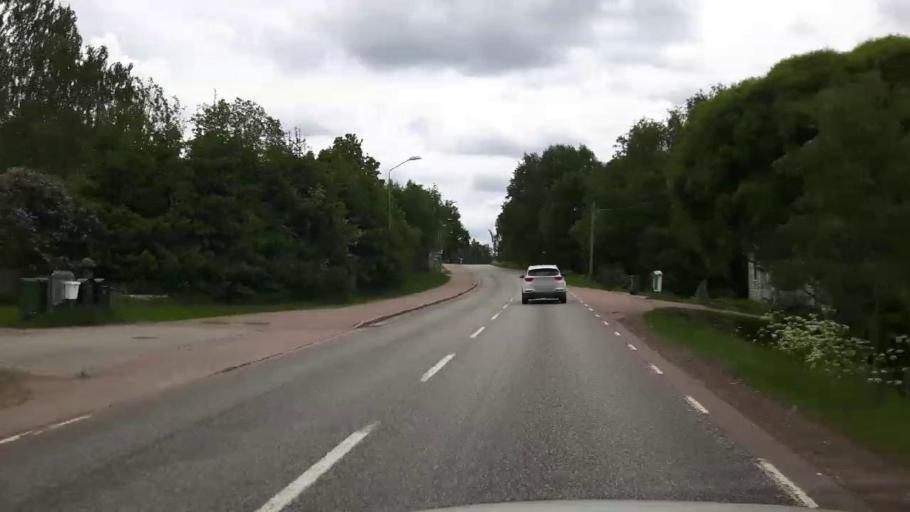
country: SE
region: Vaestmanland
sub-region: Norbergs Kommun
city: Norberg
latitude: 60.0996
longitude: 15.9294
